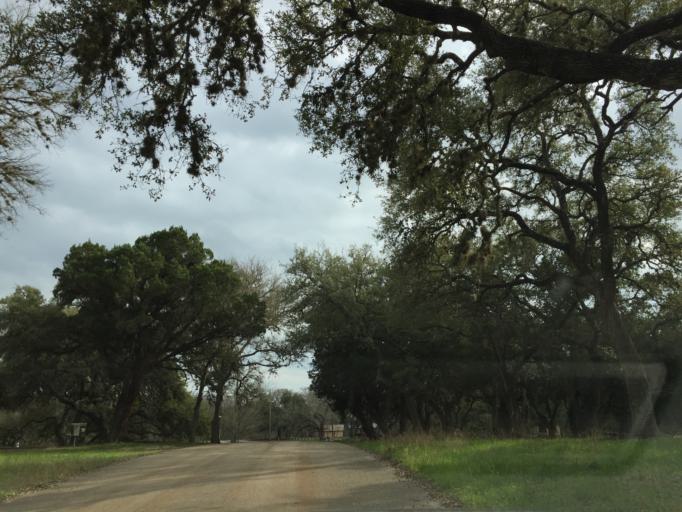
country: US
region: Texas
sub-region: Hays County
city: Dripping Springs
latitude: 30.1298
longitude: -98.0137
